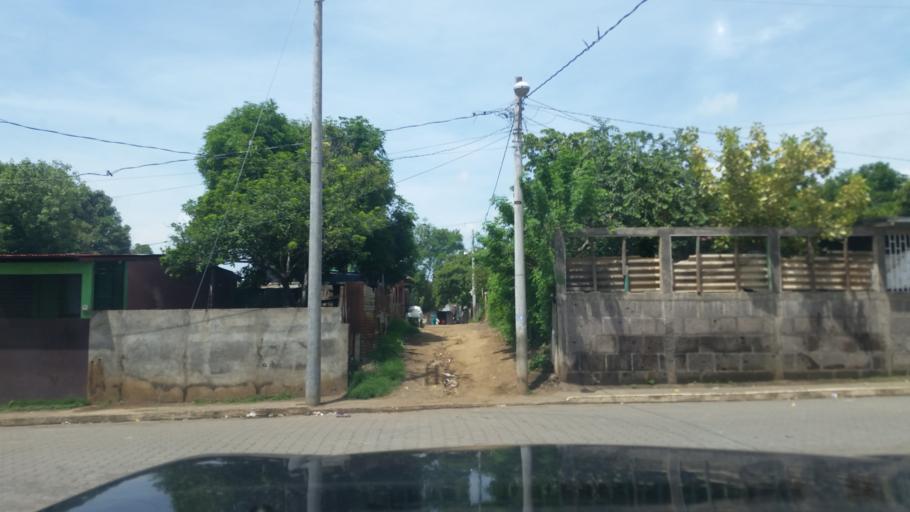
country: NI
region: Managua
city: Managua
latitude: 12.1069
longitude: -86.2403
